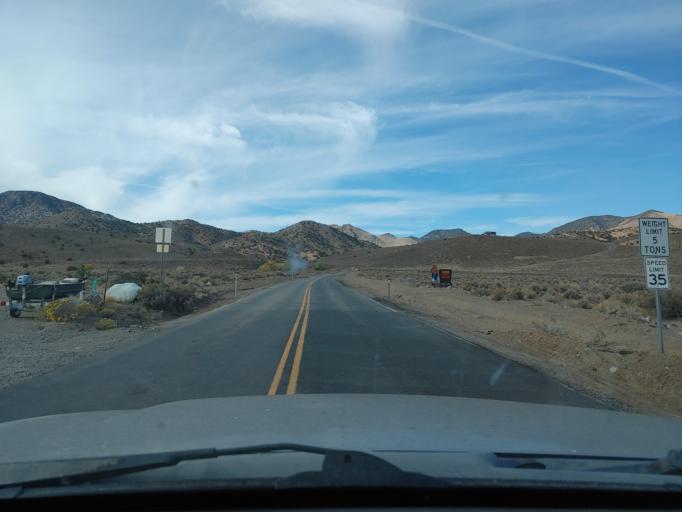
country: US
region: Nevada
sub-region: Lyon County
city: Dayton
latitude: 39.3044
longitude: -119.5573
